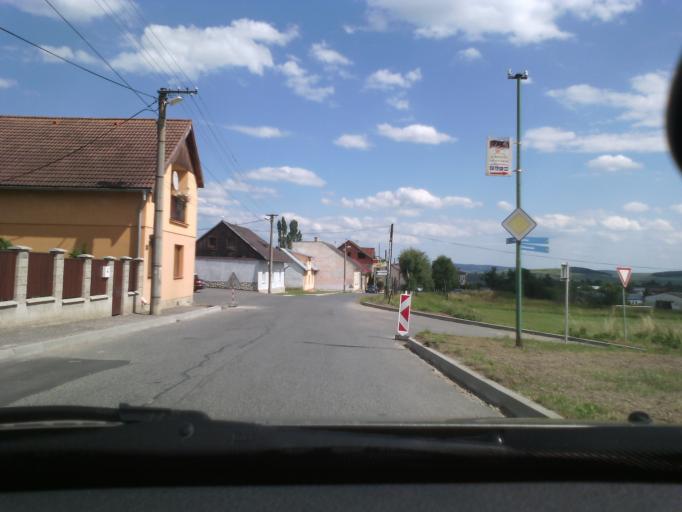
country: SK
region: Presovsky
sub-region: Okres Poprad
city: Nova Lesna
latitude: 49.1355
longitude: 20.3094
